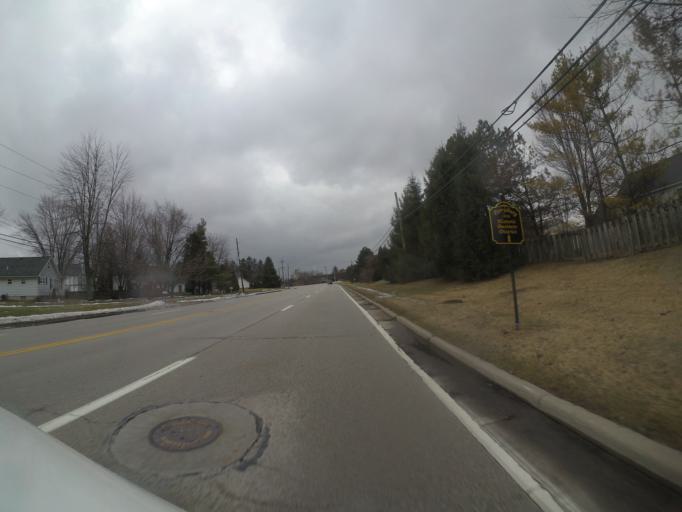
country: US
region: Ohio
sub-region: Wood County
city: Perrysburg
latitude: 41.5651
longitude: -83.6042
